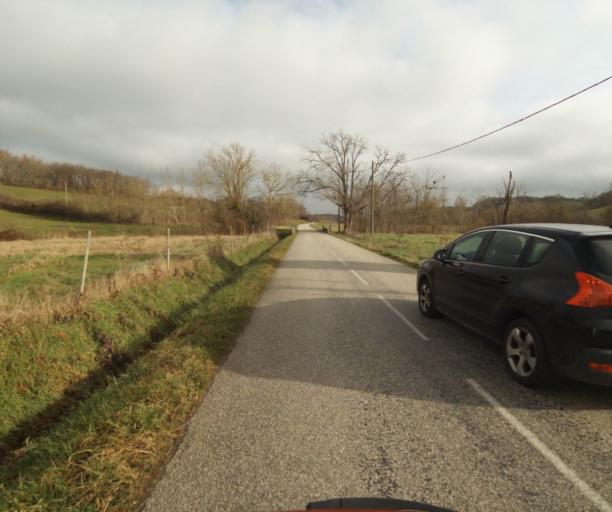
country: FR
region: Midi-Pyrenees
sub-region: Departement de l'Ariege
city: Saverdun
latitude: 43.2100
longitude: 1.5213
